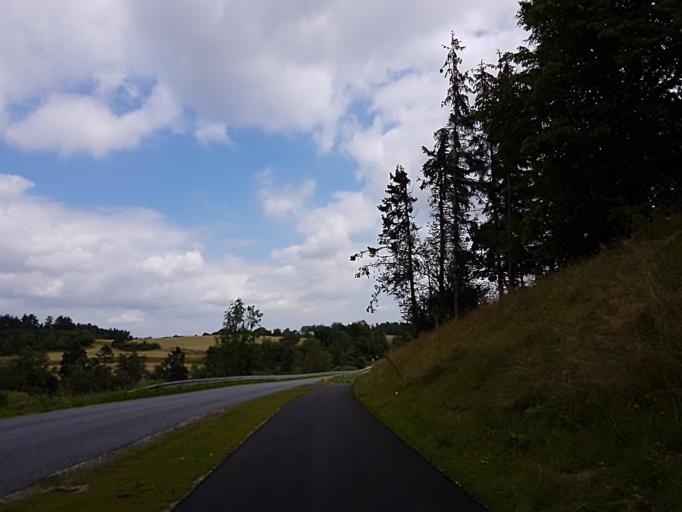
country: DK
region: Capital Region
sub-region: Egedal Kommune
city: Ganlose
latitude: 55.7993
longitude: 12.2763
